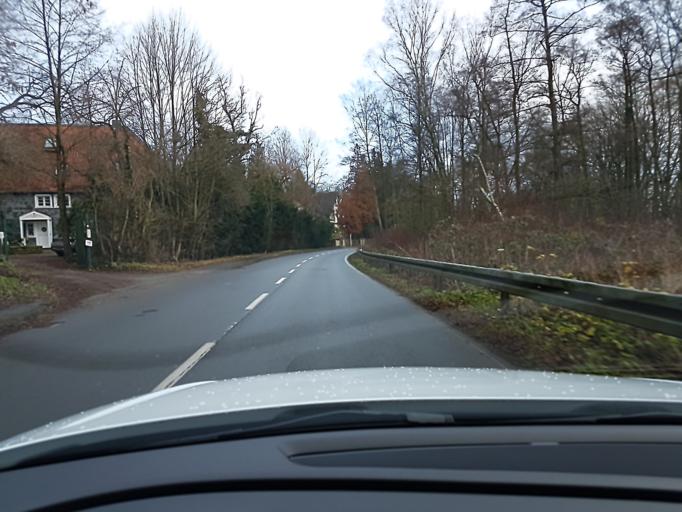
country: DE
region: North Rhine-Westphalia
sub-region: Regierungsbezirk Dusseldorf
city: Essen
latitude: 51.4026
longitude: 7.0027
